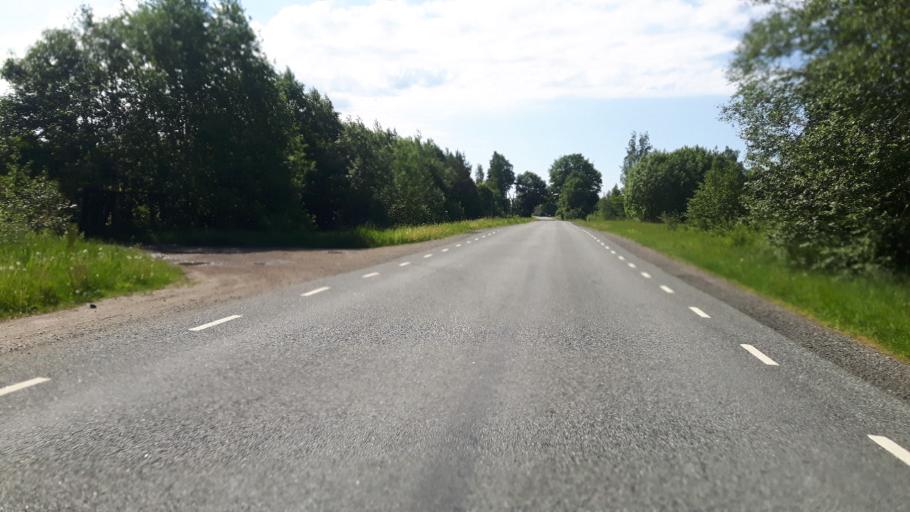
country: EE
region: Paernumaa
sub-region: Vaendra vald (alev)
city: Vandra
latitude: 58.6612
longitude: 25.0239
